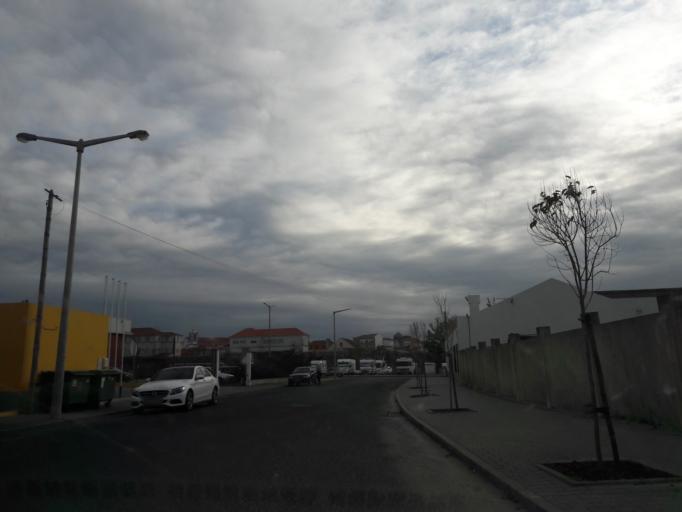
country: PT
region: Leiria
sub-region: Peniche
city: Peniche
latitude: 39.3585
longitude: -9.3763
